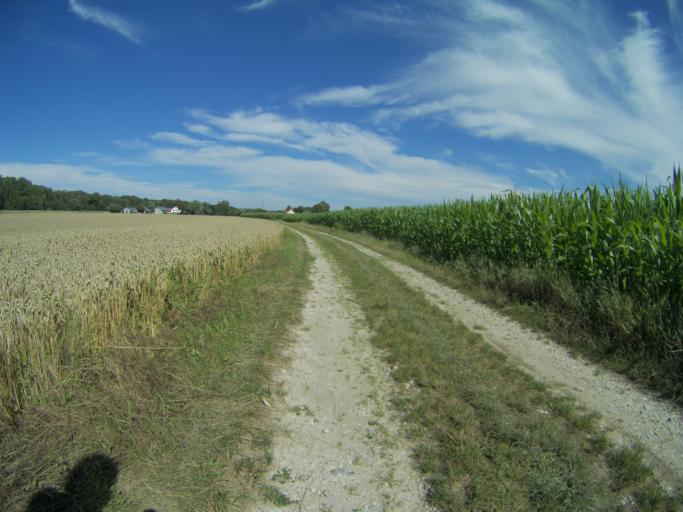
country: DE
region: Bavaria
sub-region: Upper Bavaria
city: Marzling
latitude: 48.4017
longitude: 11.8152
